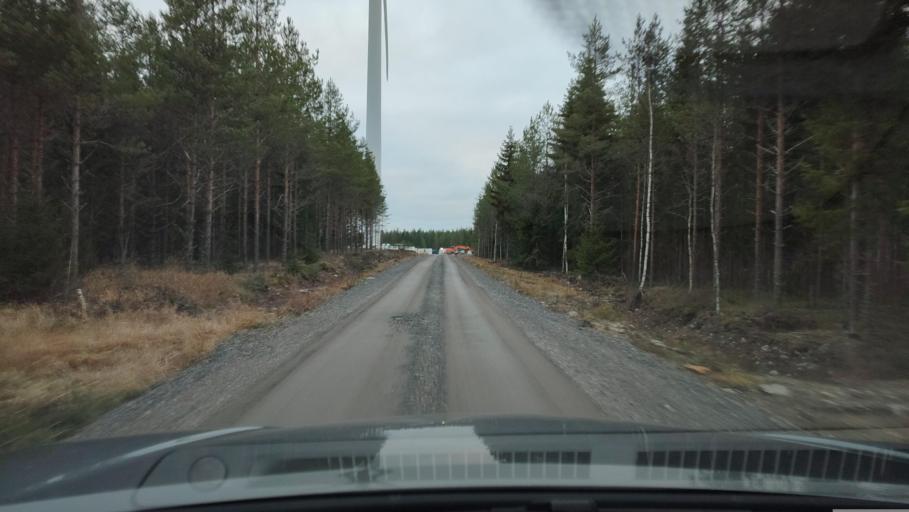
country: FI
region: Southern Ostrobothnia
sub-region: Suupohja
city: Karijoki
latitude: 62.1861
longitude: 21.5629
